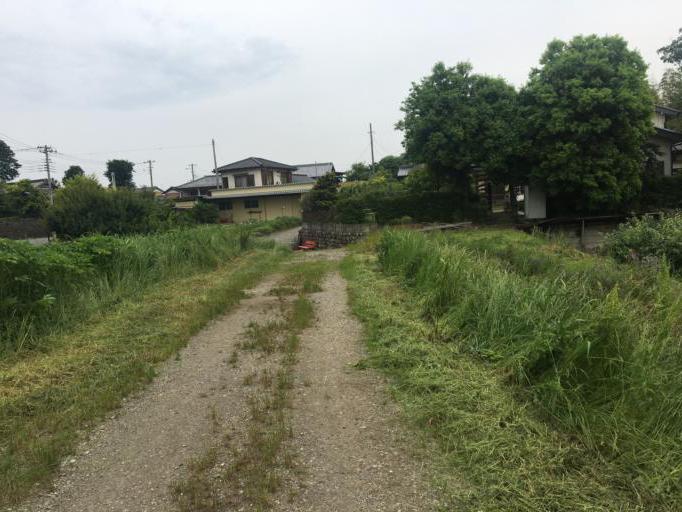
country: JP
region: Saitama
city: Sakado
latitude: 36.0148
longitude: 139.4384
